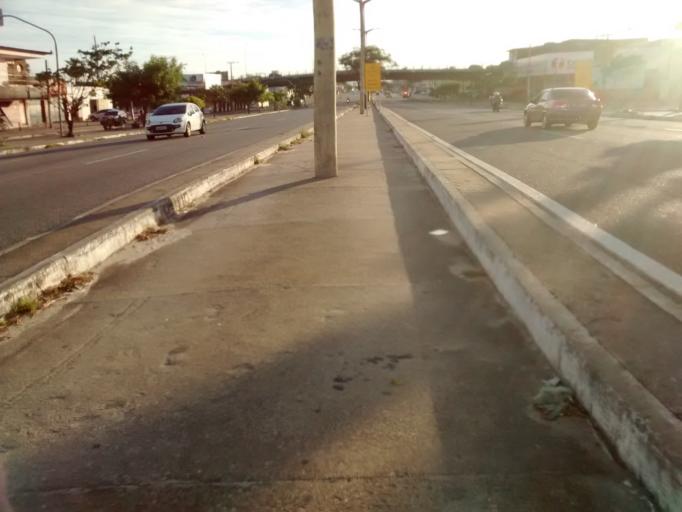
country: BR
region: Ceara
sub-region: Fortaleza
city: Fortaleza
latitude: -3.7386
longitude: -38.5838
